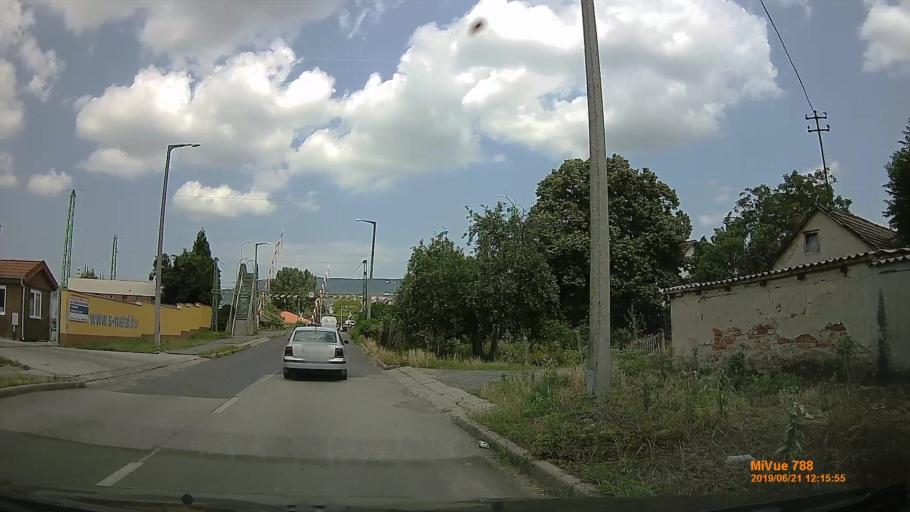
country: HU
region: Baranya
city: Pecs
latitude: 46.0633
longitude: 18.2134
